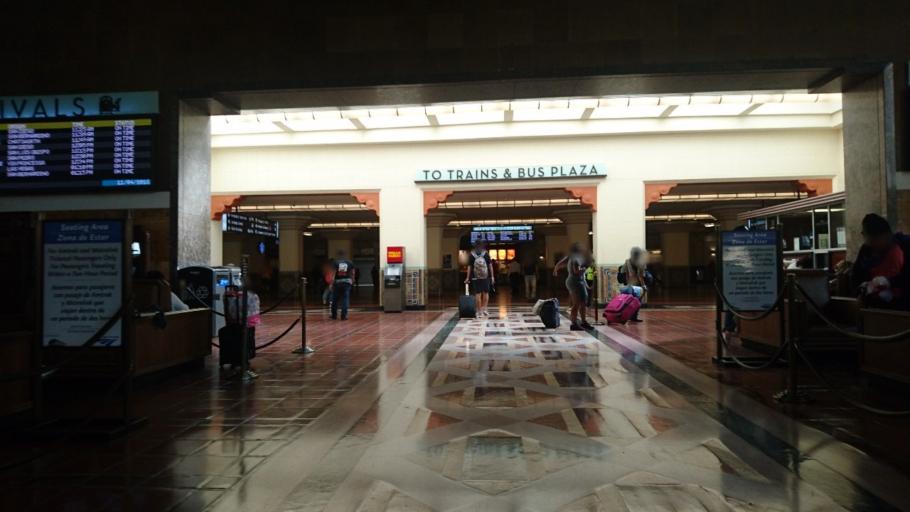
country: US
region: California
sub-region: Los Angeles County
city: Los Angeles
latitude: 34.0560
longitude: -118.2361
